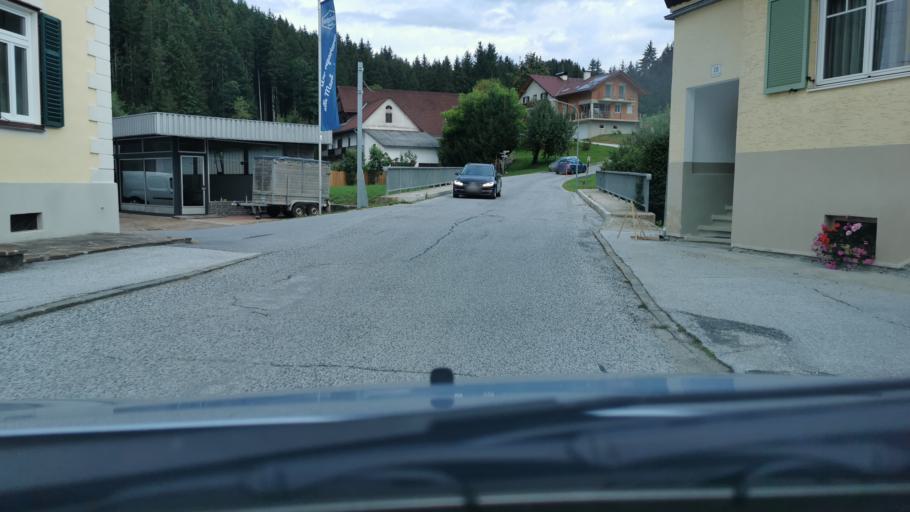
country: AT
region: Styria
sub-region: Politischer Bezirk Weiz
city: Birkfeld
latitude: 47.3589
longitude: 15.6896
